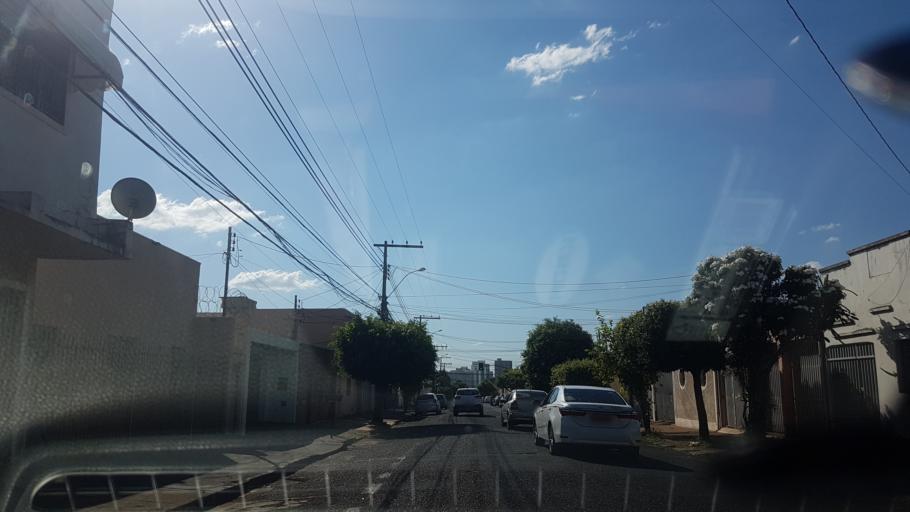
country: BR
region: Minas Gerais
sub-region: Uberlandia
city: Uberlandia
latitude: -18.9107
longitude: -48.2836
